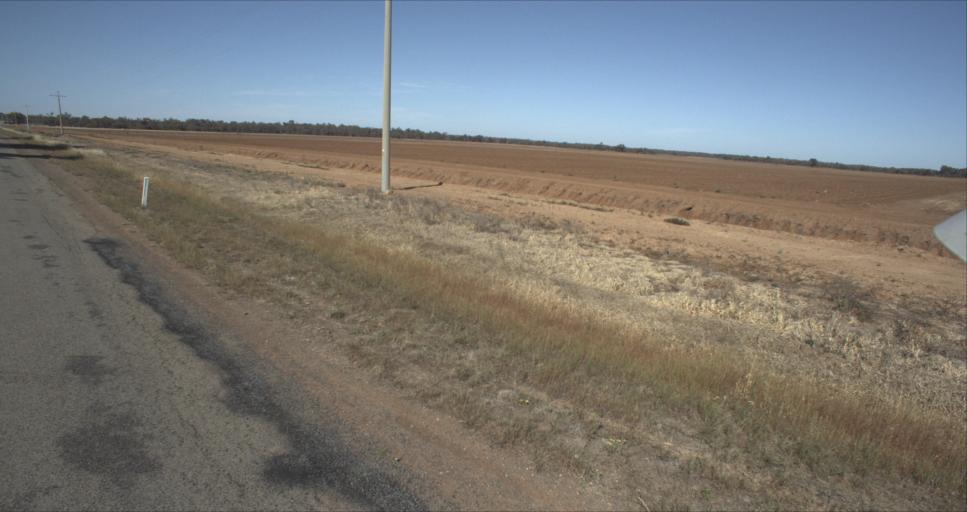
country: AU
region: New South Wales
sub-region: Leeton
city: Leeton
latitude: -34.5977
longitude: 146.2583
